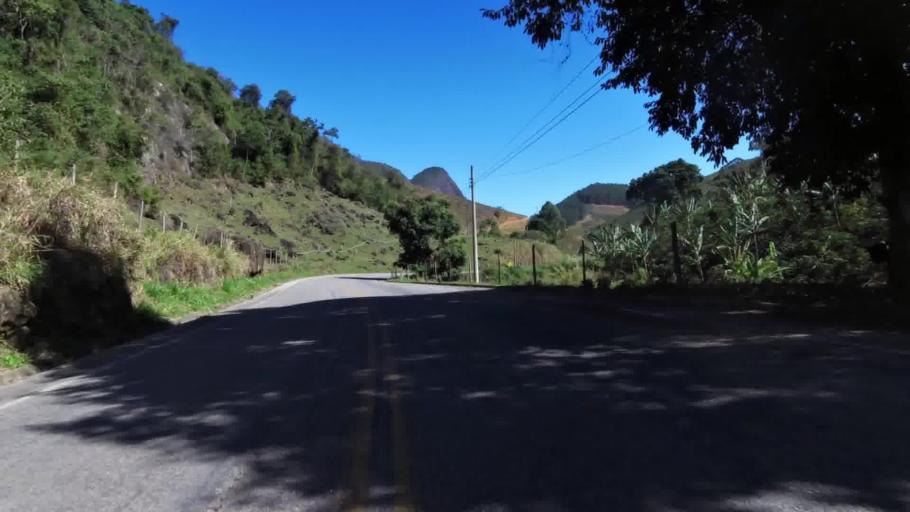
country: BR
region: Espirito Santo
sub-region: Iconha
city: Iconha
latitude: -20.7355
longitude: -40.8754
